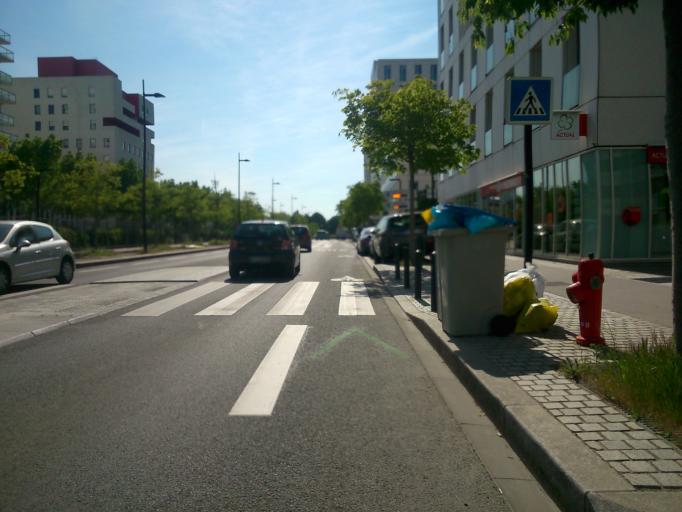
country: FR
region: Pays de la Loire
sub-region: Departement de la Loire-Atlantique
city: Nantes
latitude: 47.2154
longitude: -1.5363
